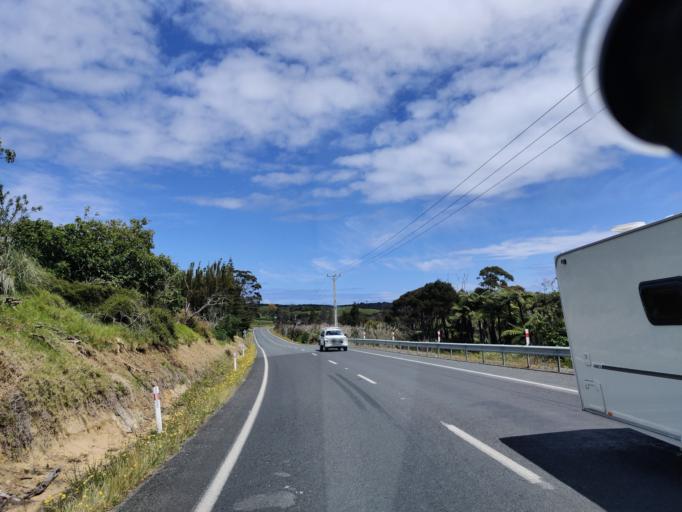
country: NZ
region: Northland
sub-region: Far North District
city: Kaitaia
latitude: -35.0109
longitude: 173.2065
